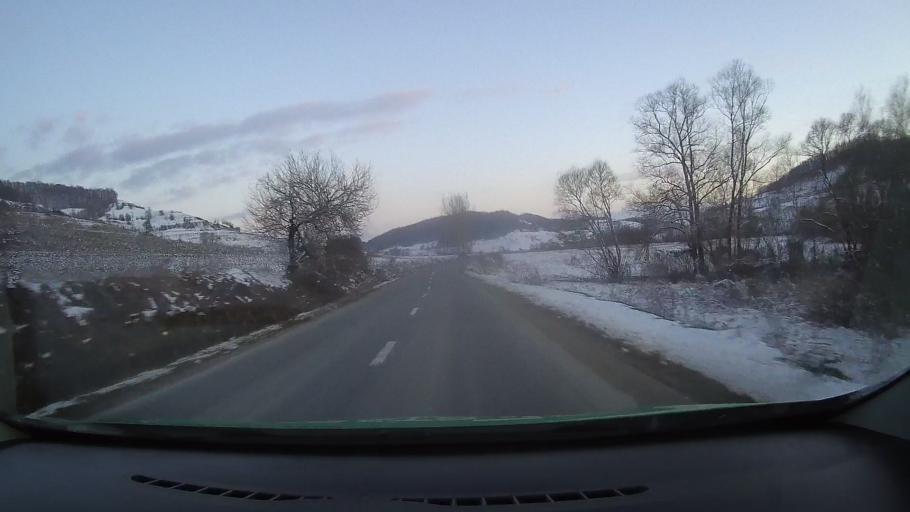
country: RO
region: Sibiu
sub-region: Comuna Alma
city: Alma
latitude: 46.1983
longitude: 24.4698
